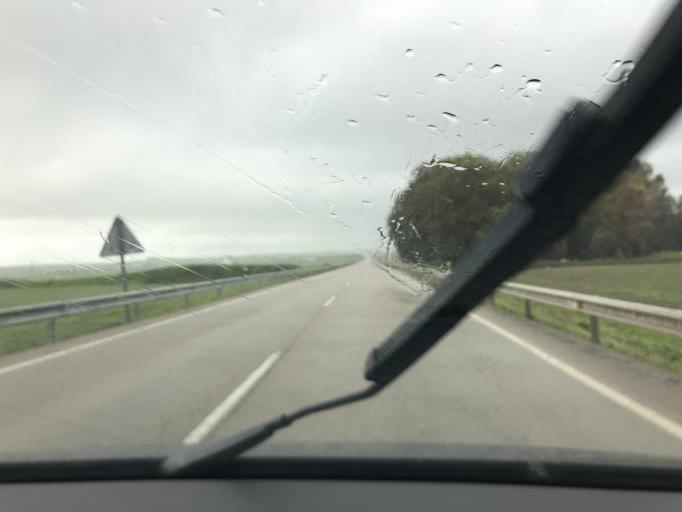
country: ES
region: Andalusia
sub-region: Provincia de Sevilla
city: Fuentes de Andalucia
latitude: 37.4341
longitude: -5.2648
